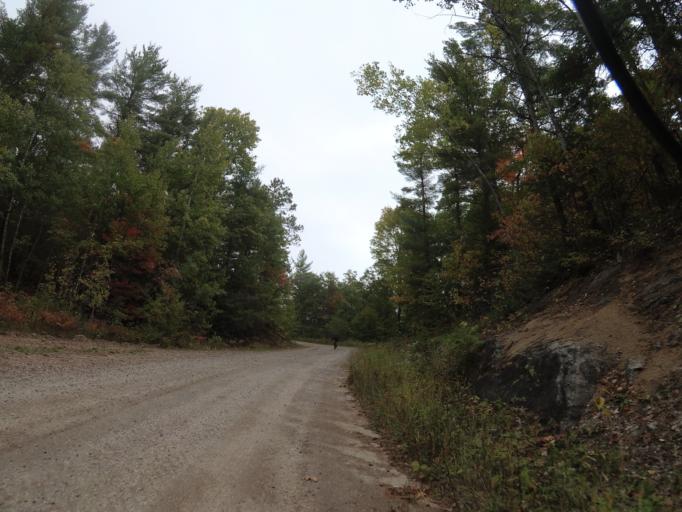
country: CA
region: Ontario
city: Renfrew
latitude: 45.2071
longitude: -77.0748
